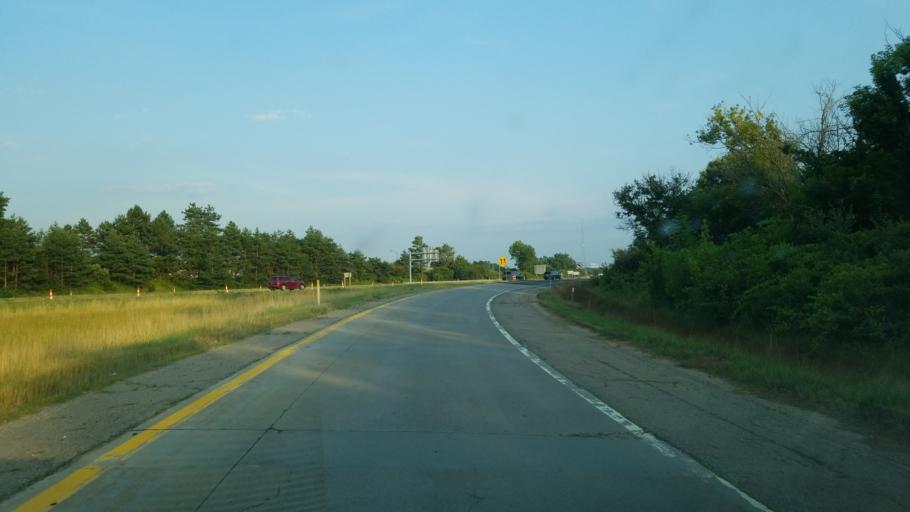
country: US
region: Michigan
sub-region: Ingham County
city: Holt
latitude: 42.6876
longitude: -84.5040
